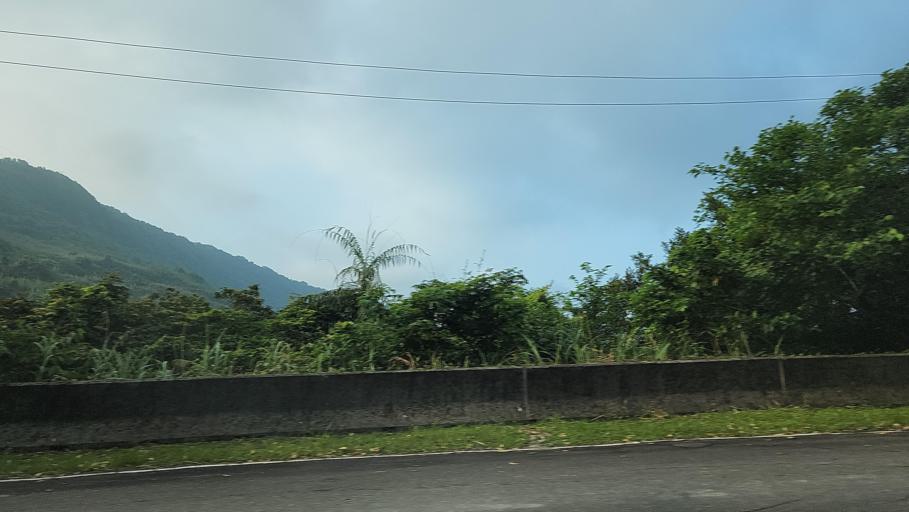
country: TW
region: Taiwan
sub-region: Keelung
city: Keelung
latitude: 25.1551
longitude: 121.6465
